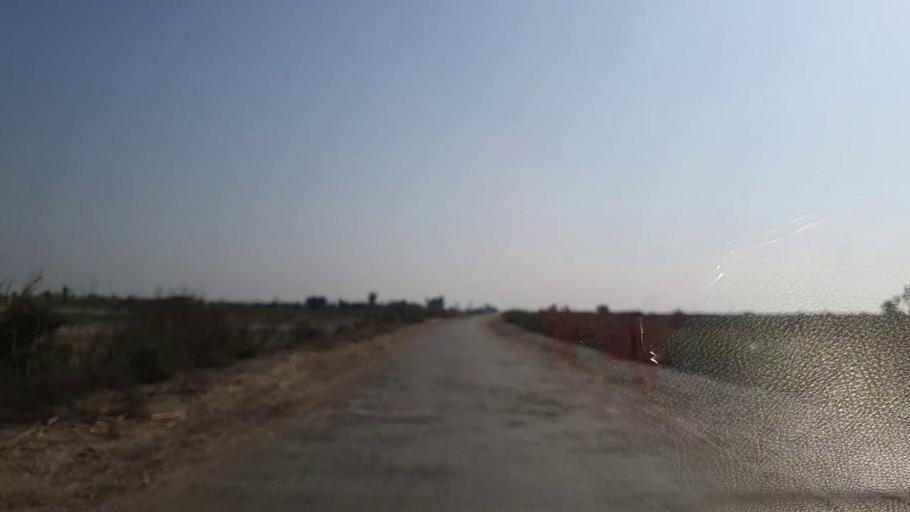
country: PK
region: Sindh
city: Sanghar
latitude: 25.9982
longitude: 69.0239
